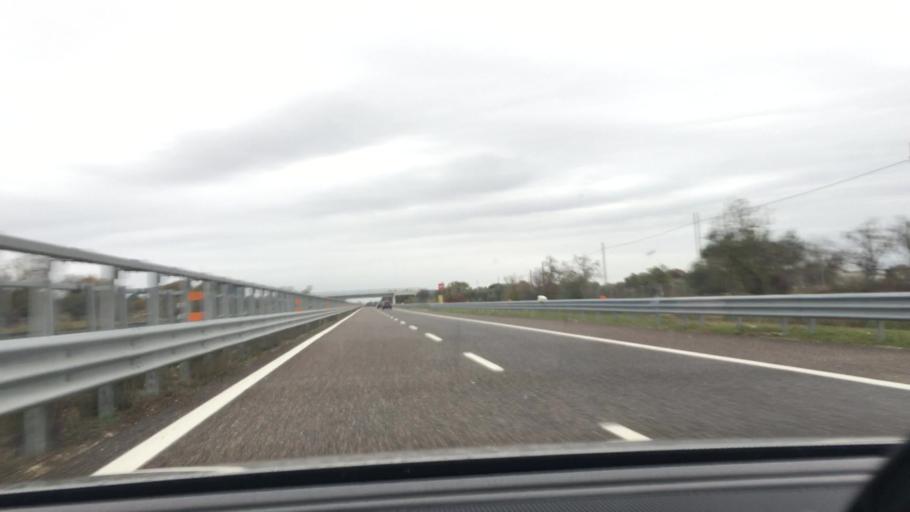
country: IT
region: Apulia
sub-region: Provincia di Bari
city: Gioia del Colle
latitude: 40.7457
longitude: 16.9146
